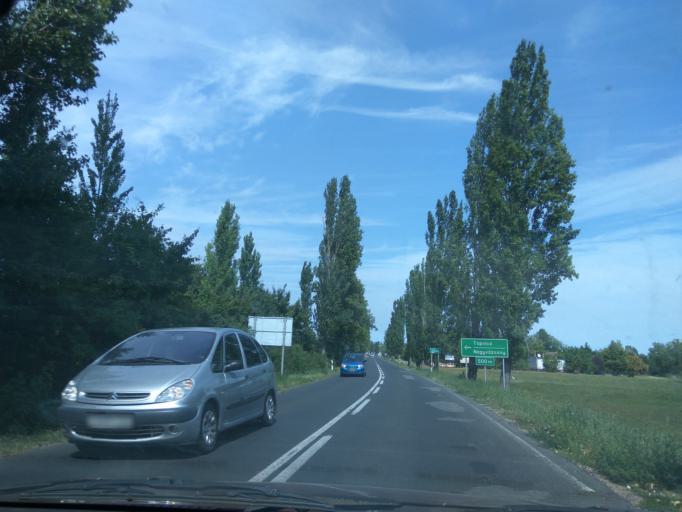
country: HU
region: Veszprem
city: Zanka
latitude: 46.8684
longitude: 17.6789
